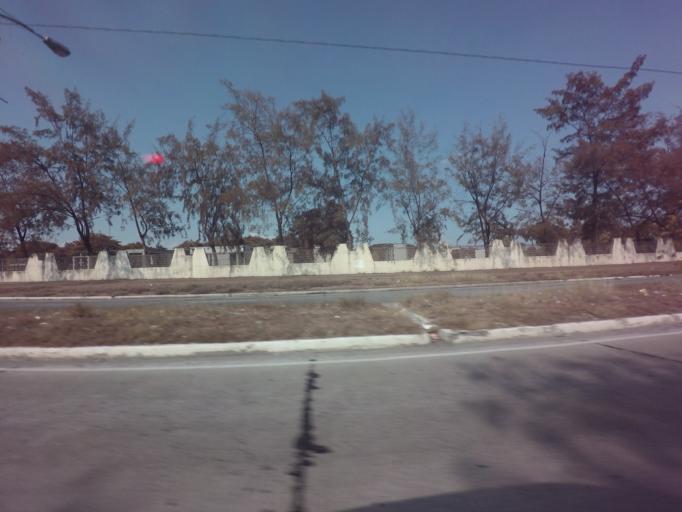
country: PH
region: Calabarzon
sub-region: Province of Rizal
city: Pateros
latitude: 14.5205
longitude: 121.0468
